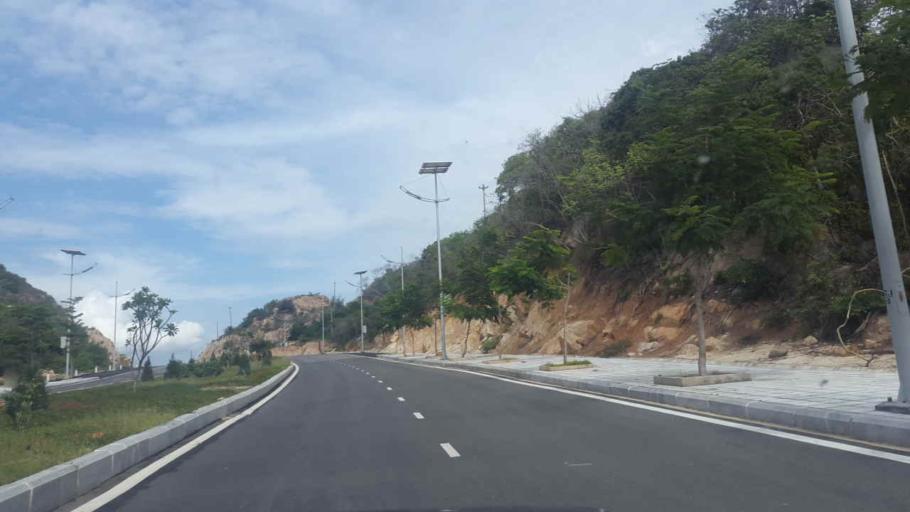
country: VN
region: Khanh Hoa
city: Cam Ranh
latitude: 11.8667
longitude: 109.2515
